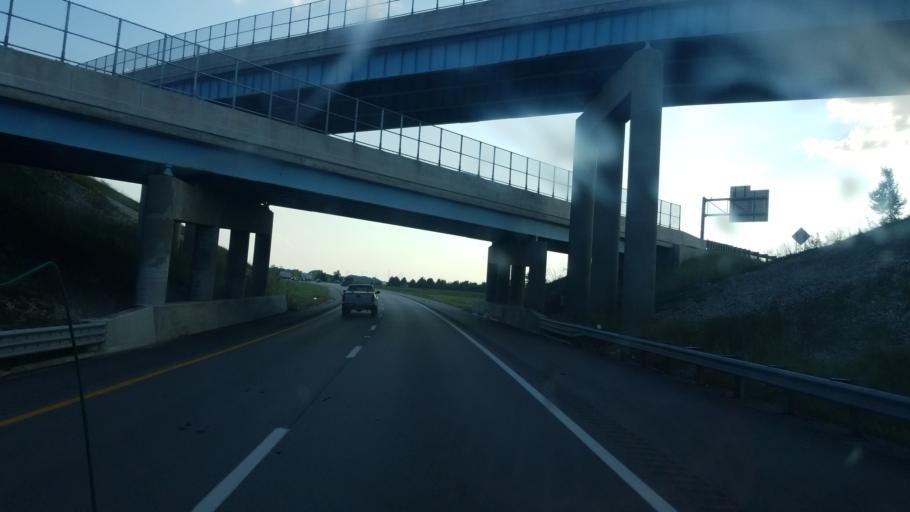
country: US
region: Ohio
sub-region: Wood County
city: Perrysburg
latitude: 41.5323
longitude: -83.6212
